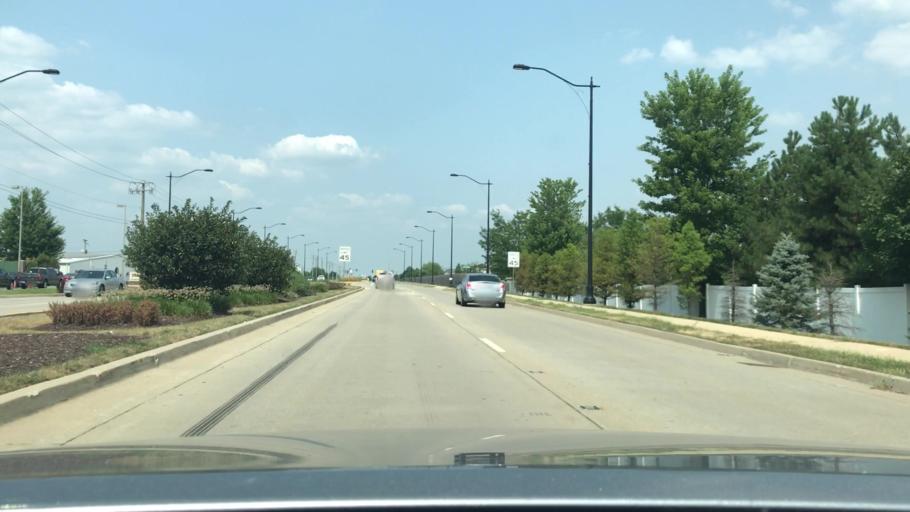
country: US
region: Illinois
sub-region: Will County
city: Shorewood
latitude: 41.5423
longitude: -88.1994
